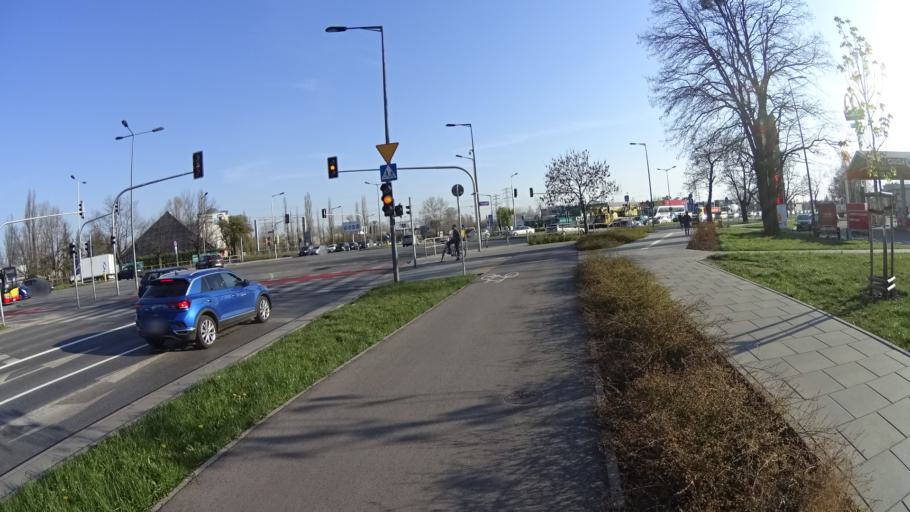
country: PL
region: Masovian Voivodeship
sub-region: Warszawa
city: Bemowo
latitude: 52.2207
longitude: 20.9163
